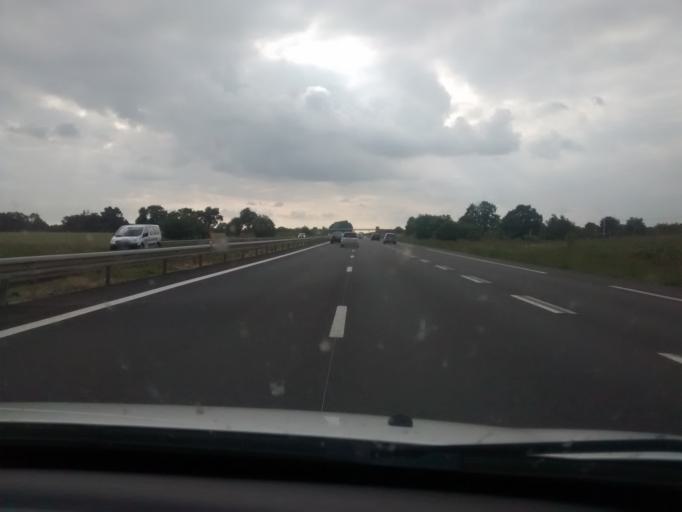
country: FR
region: Pays de la Loire
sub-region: Departement de la Mayenne
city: Sainte-Suzanne
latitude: 48.0239
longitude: -0.3292
